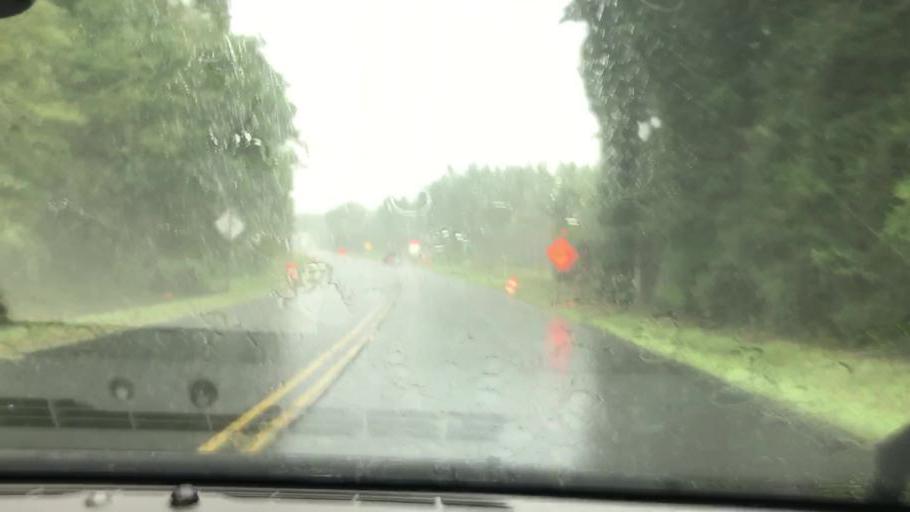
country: US
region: Georgia
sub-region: Clay County
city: Fort Gaines
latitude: 31.5528
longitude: -85.0193
